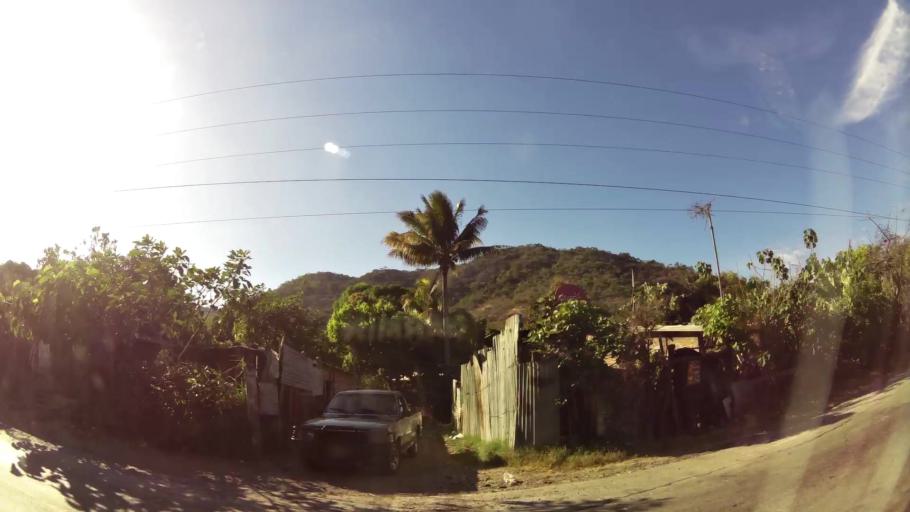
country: SV
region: Santa Ana
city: Santa Ana
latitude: 14.0501
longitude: -89.5166
